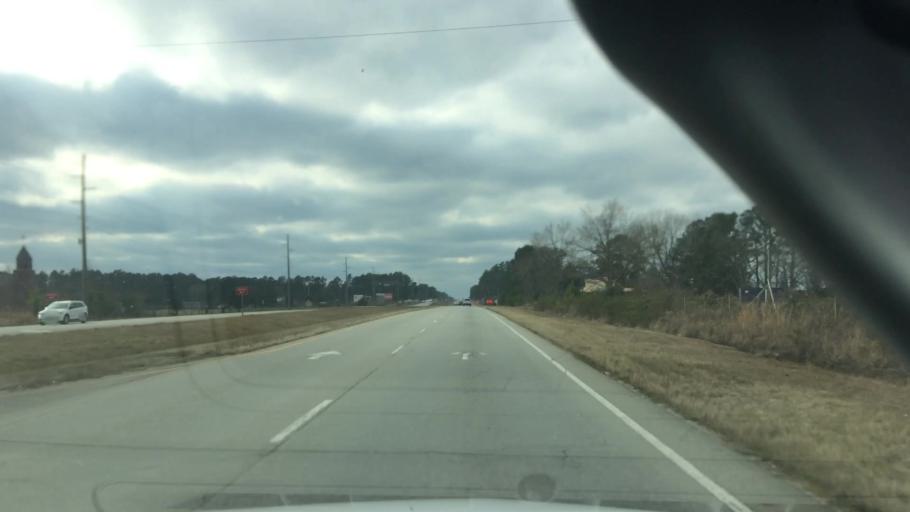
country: US
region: North Carolina
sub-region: Brunswick County
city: Shallotte
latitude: 33.9577
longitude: -78.4290
